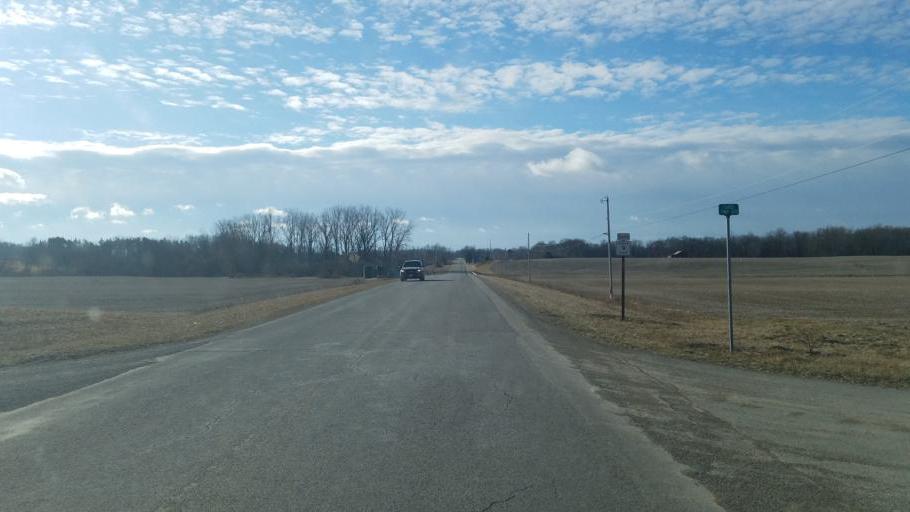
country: US
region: Ohio
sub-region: Morrow County
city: Mount Gilead
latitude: 40.5311
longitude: -82.8635
